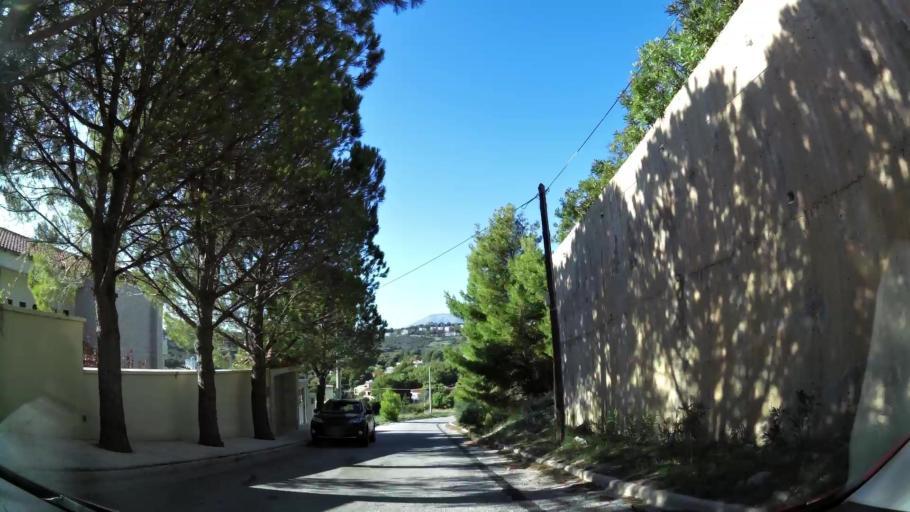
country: GR
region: Attica
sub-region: Nomarchia Anatolikis Attikis
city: Dhrafi
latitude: 38.0228
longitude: 23.9073
